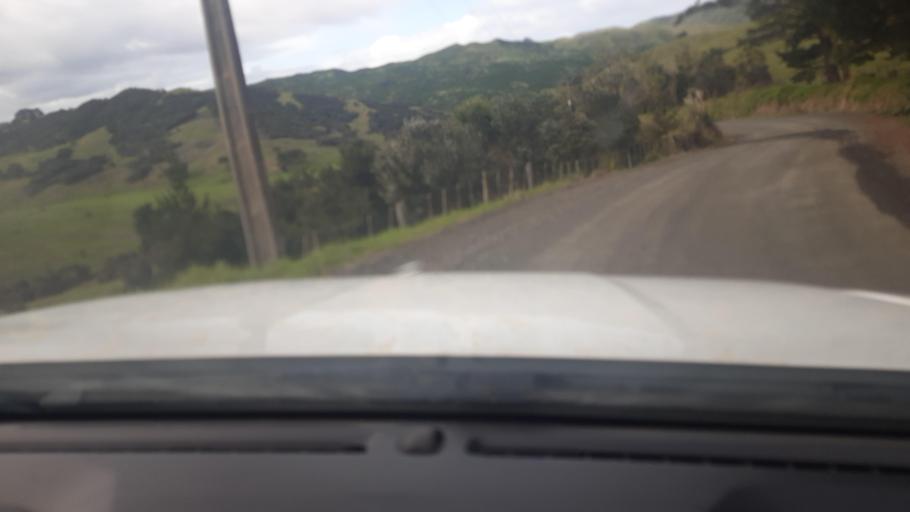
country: NZ
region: Northland
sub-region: Far North District
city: Ahipara
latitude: -35.2824
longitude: 173.2063
